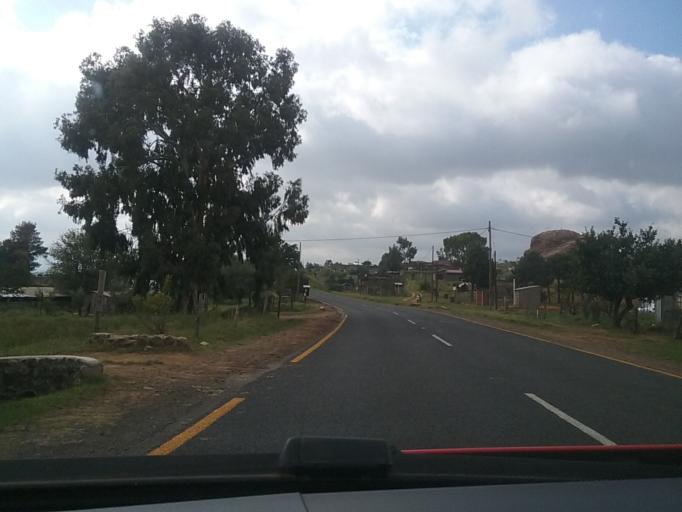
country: LS
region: Berea
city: Teyateyaneng
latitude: -29.1582
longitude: 27.7558
